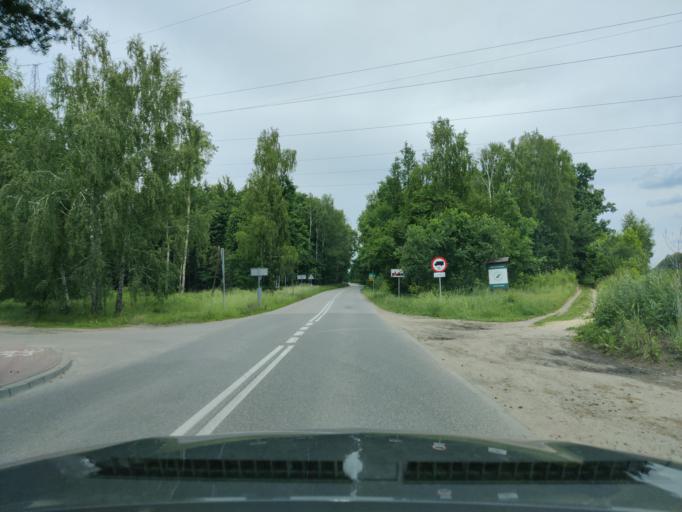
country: PL
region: Masovian Voivodeship
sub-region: Powiat wyszkowski
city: Wyszkow
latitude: 52.6214
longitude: 21.4522
